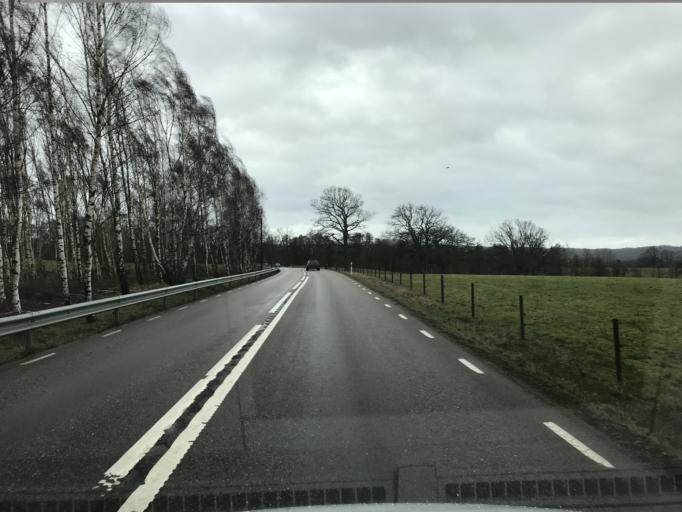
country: SE
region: Skane
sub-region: Klippans Kommun
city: Klippan
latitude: 56.1116
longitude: 13.1786
